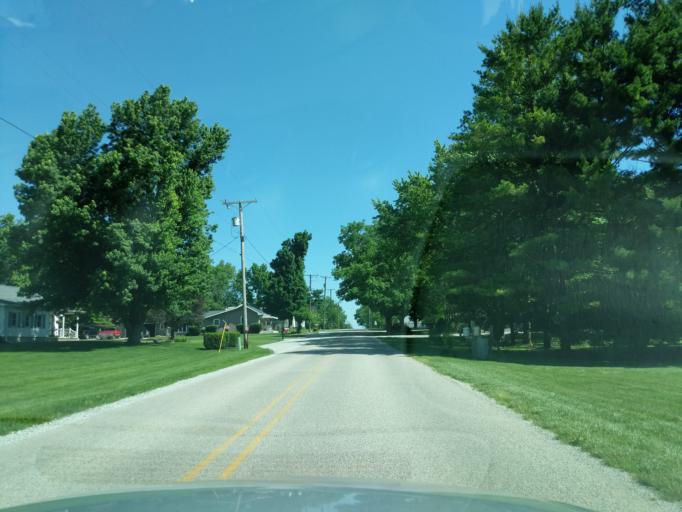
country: US
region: Indiana
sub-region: Huntington County
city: Warren
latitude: 40.7481
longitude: -85.5070
